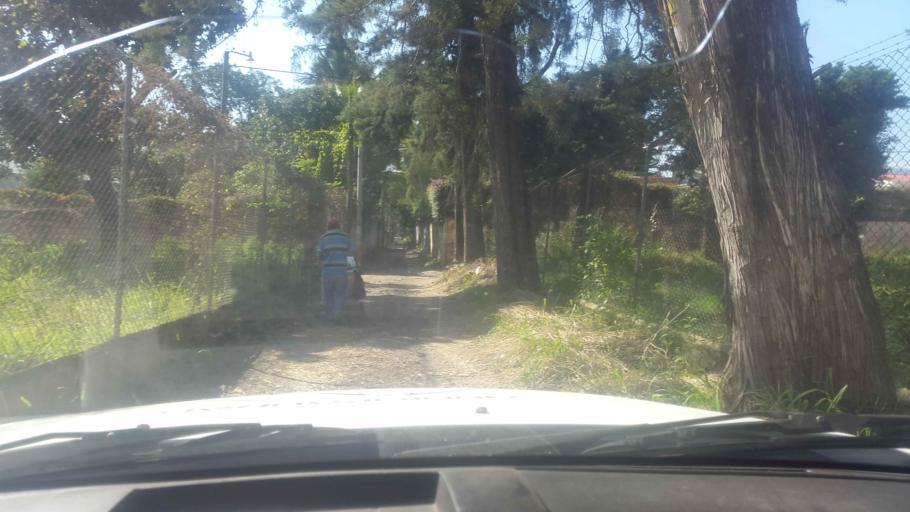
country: GT
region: Guatemala
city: Petapa
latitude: 14.5124
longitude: -90.5369
